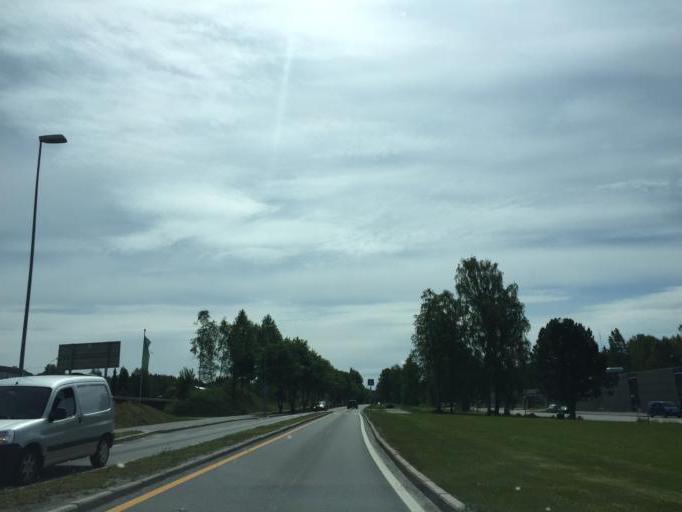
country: NO
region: Hedmark
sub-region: Kongsvinger
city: Kongsvinger
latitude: 60.2018
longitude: 11.9785
